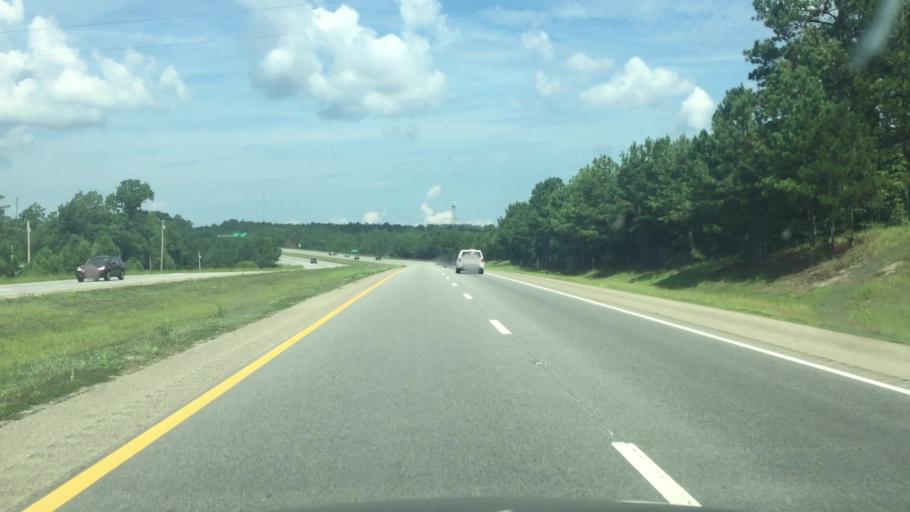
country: US
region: North Carolina
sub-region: Richmond County
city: Hamlet
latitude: 34.8660
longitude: -79.6397
